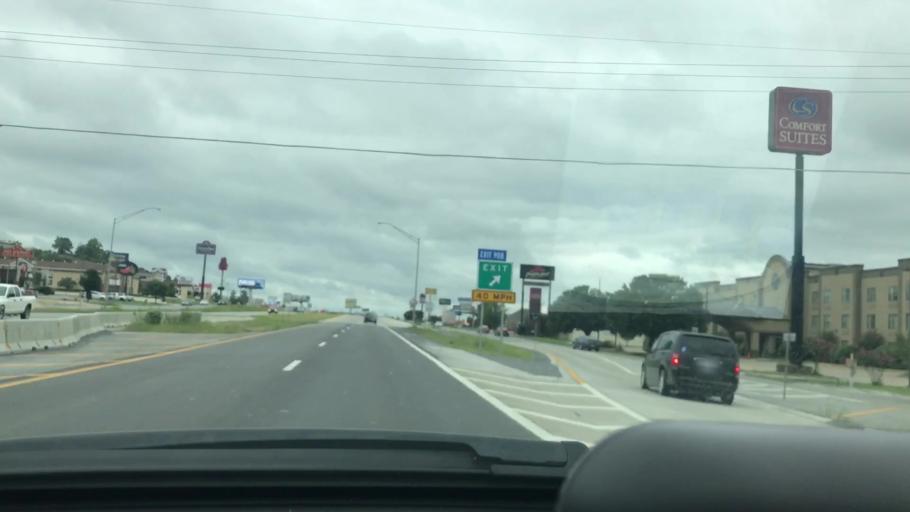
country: US
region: Oklahoma
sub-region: Pittsburg County
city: McAlester
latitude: 34.9128
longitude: -95.7452
